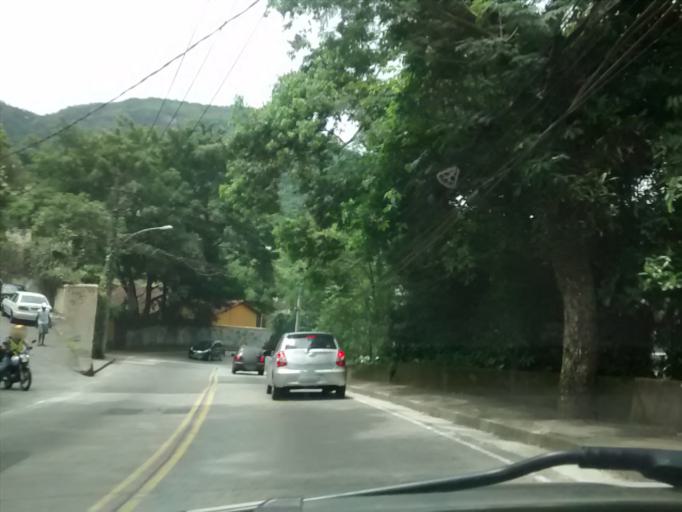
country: BR
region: Rio de Janeiro
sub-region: Rio De Janeiro
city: Rio de Janeiro
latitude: -22.9711
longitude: -43.2829
